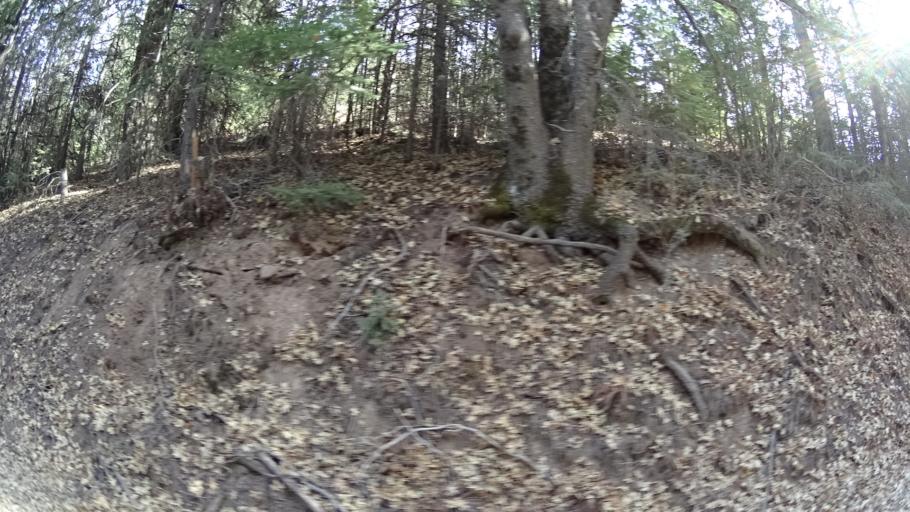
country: US
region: California
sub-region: Siskiyou County
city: Weed
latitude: 41.4405
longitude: -122.4247
